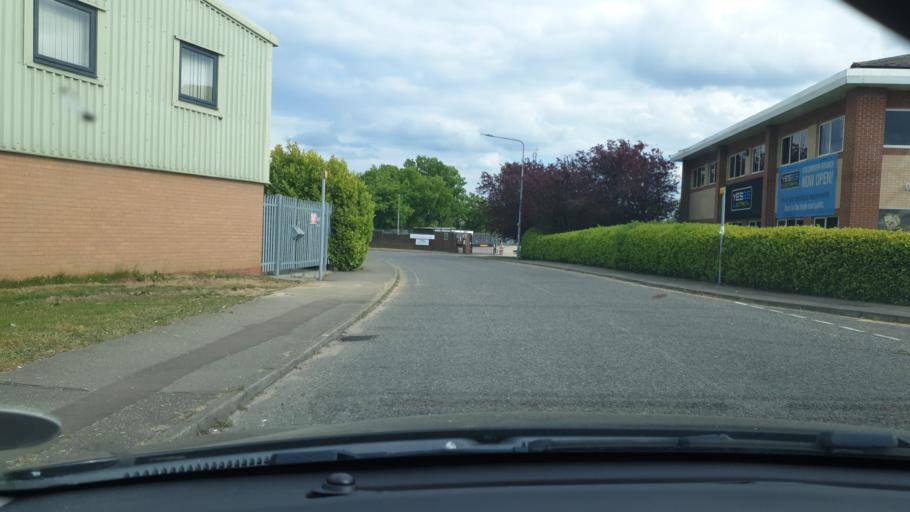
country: GB
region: England
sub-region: Essex
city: Colchester
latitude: 51.9193
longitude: 0.9237
